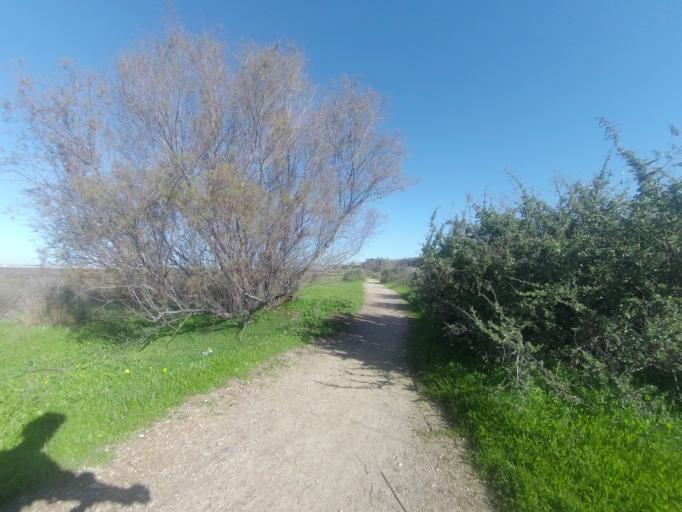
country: ES
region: Andalusia
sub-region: Provincia de Huelva
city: Palos de la Frontera
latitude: 37.2351
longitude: -6.8948
